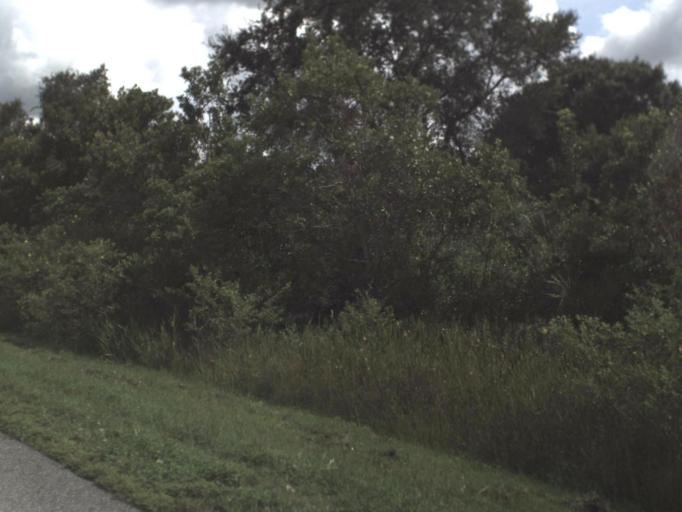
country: US
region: Florida
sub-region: Sarasota County
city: Warm Mineral Springs
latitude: 27.1979
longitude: -82.2277
